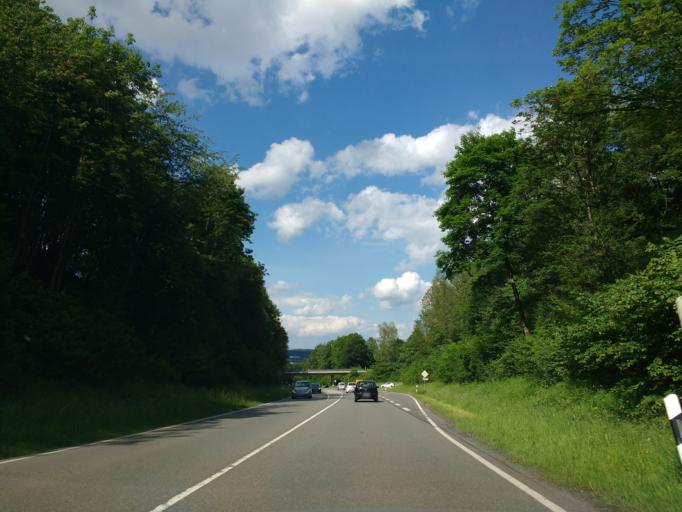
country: DE
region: Hesse
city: Battenberg
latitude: 51.0091
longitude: 8.6505
